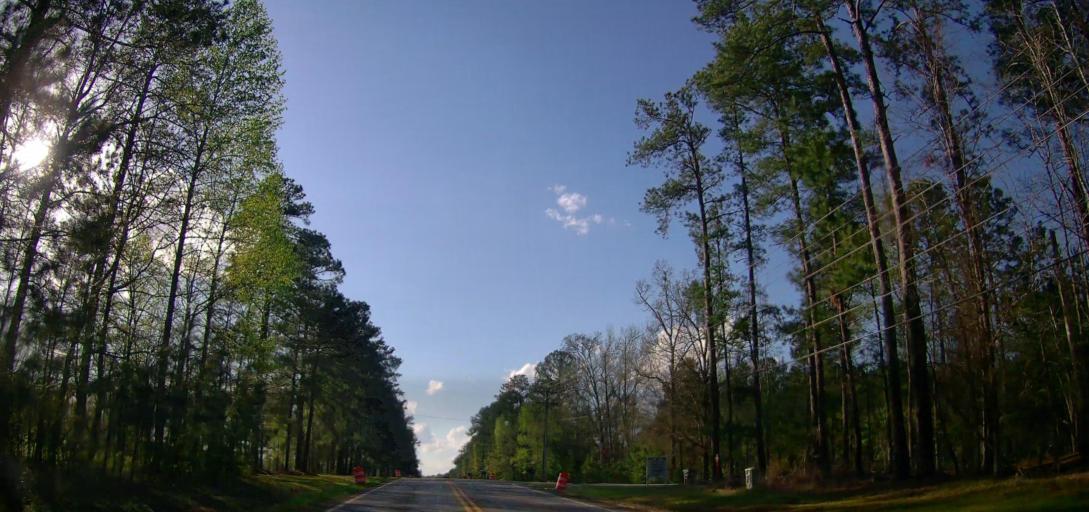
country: US
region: Georgia
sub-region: Putnam County
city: Eatonton
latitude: 33.1689
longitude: -83.3862
